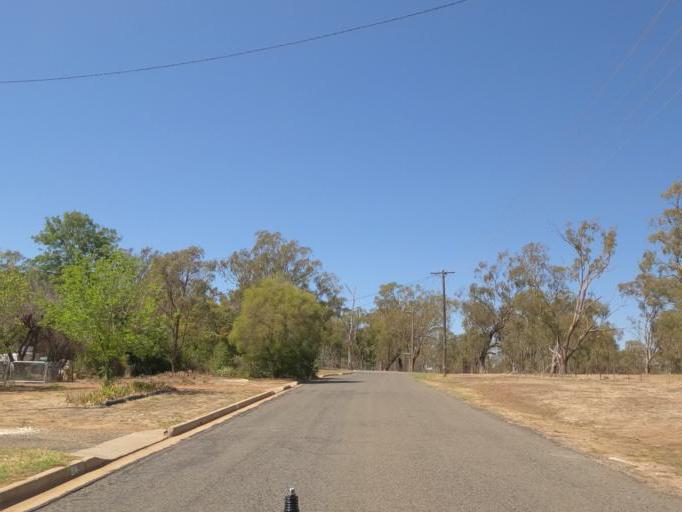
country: AU
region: New South Wales
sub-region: Corowa Shire
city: Mulwala
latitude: -35.9951
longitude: 145.9950
